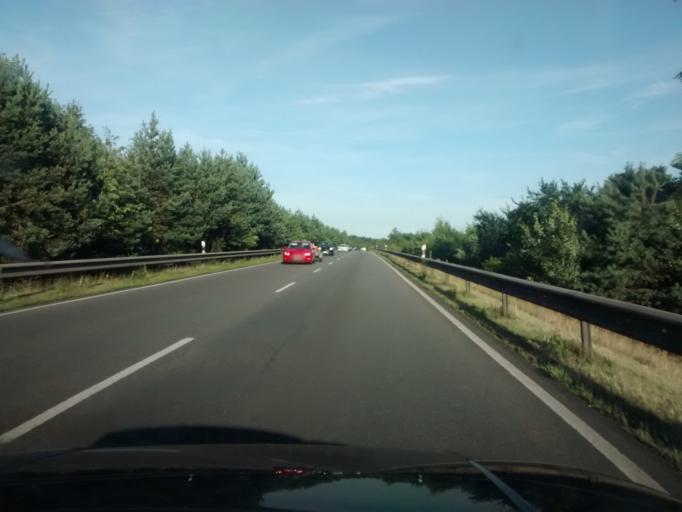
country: DE
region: Lower Saxony
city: Meppen
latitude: 52.7110
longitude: 7.3034
